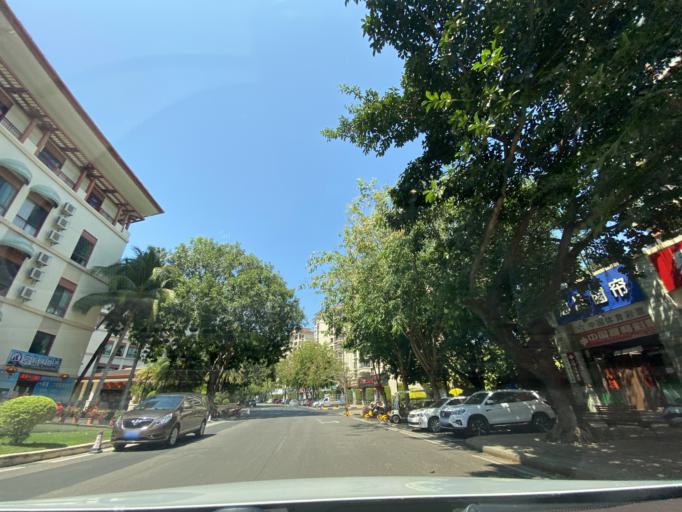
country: CN
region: Hainan
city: Yingzhou
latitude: 18.4071
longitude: 109.8503
